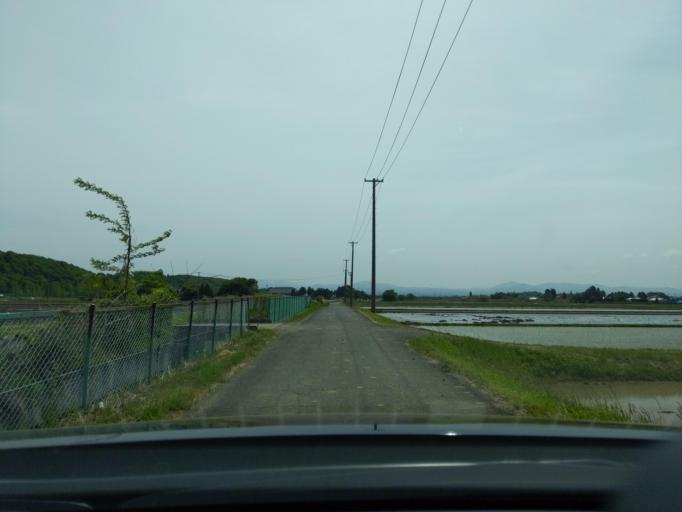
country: JP
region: Fukushima
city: Koriyama
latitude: 37.3959
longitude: 140.2917
